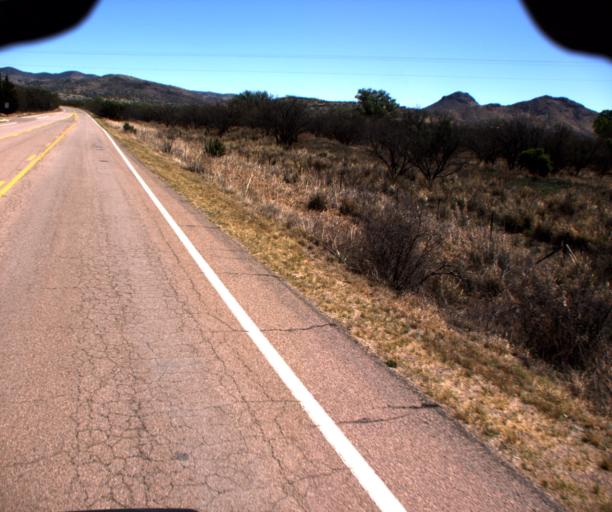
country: US
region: Arizona
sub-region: Santa Cruz County
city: Rio Rico
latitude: 31.5449
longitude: -110.7461
